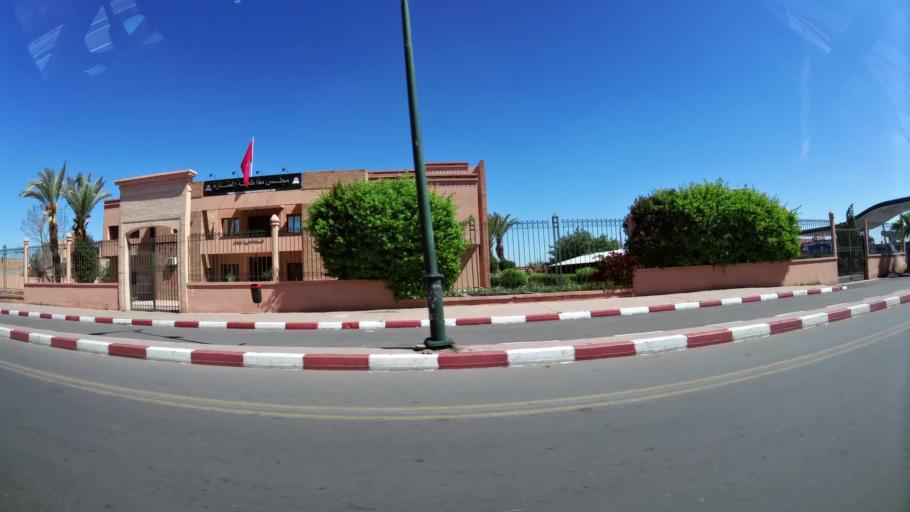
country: MA
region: Marrakech-Tensift-Al Haouz
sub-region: Marrakech
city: Marrakesh
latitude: 31.6273
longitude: -8.0355
